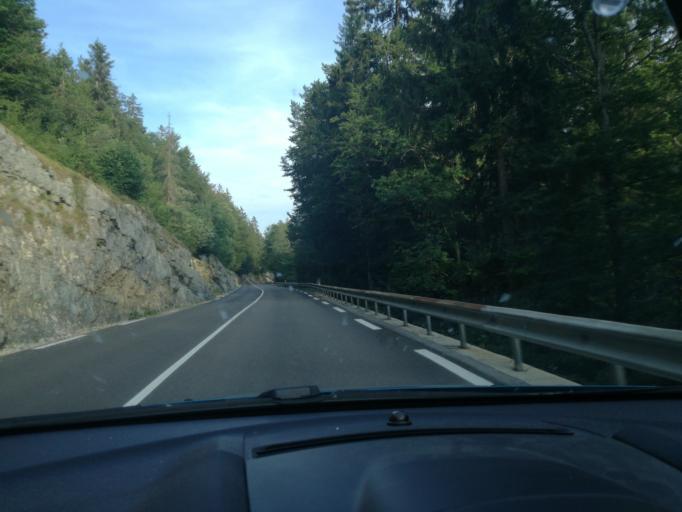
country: FR
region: Franche-Comte
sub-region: Departement du Jura
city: Morbier
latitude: 46.6254
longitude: 5.9559
